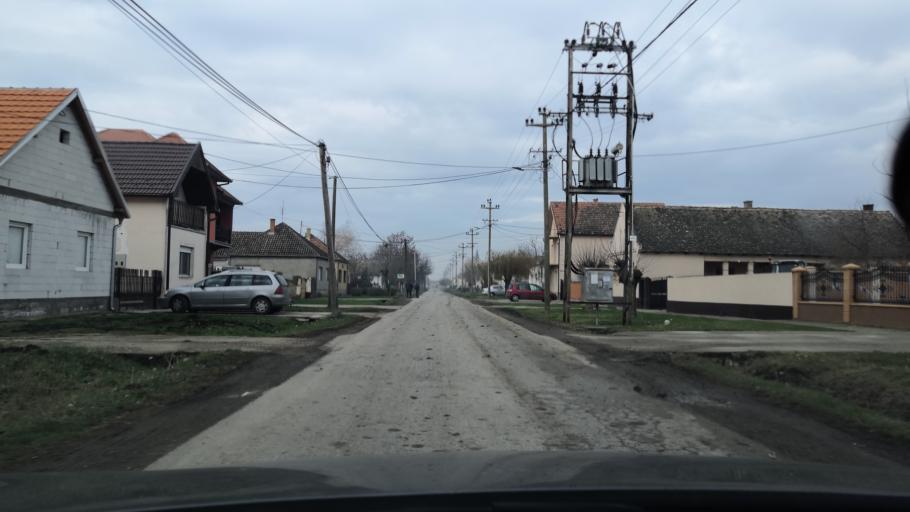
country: RS
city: Ugrinovci
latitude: 44.8876
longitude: 20.1444
